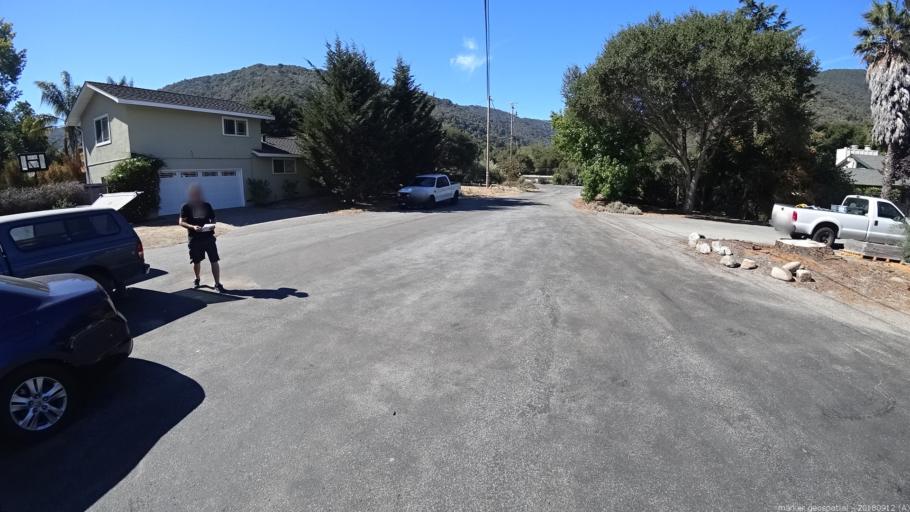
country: US
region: California
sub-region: Monterey County
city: Carmel Valley Village
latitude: 36.4910
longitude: -121.7504
